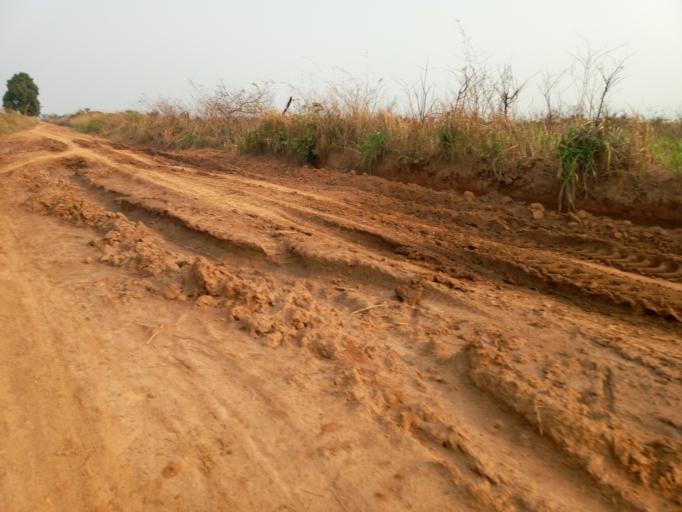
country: CD
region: Bandundu
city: Bandundu
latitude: -3.4105
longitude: 17.5972
